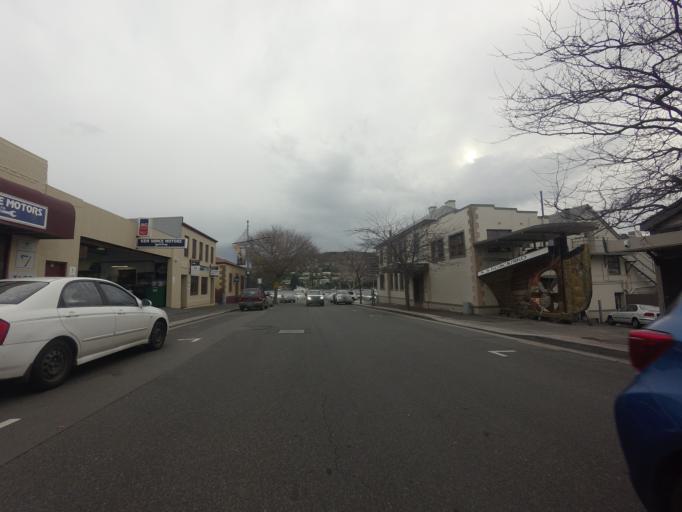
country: AU
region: Tasmania
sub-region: Clarence
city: Bellerive
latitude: -42.8745
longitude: 147.3659
